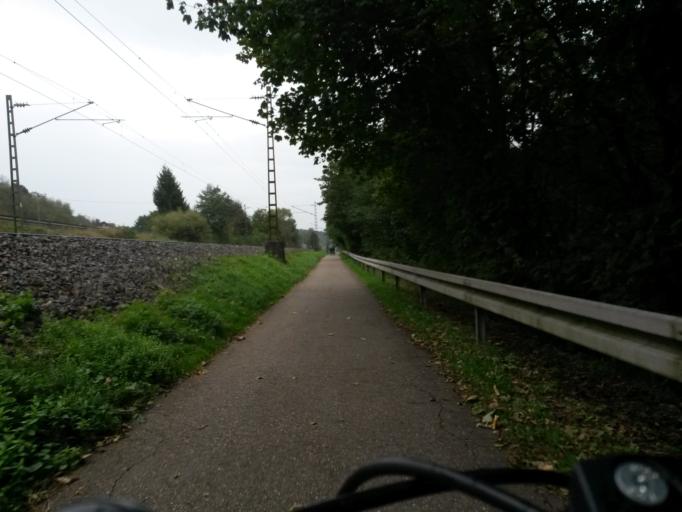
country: DE
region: Baden-Wuerttemberg
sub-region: Karlsruhe Region
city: Konigsbach-Stein
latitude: 48.9599
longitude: 8.5600
